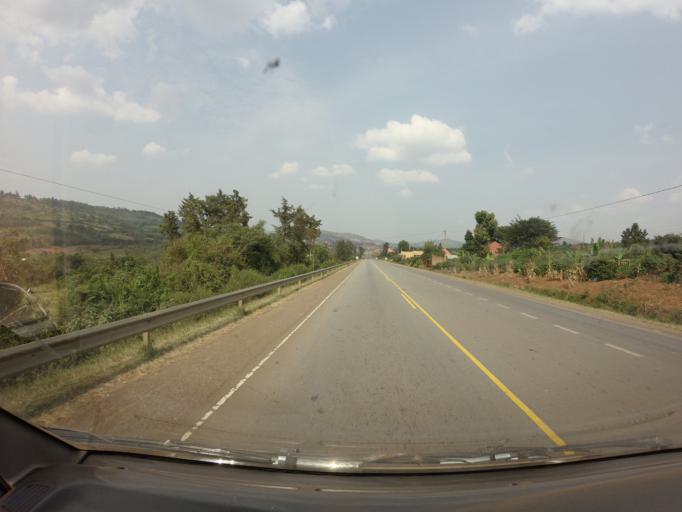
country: UG
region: Central Region
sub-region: Lwengo District
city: Lwengo
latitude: -0.3820
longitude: 31.3064
